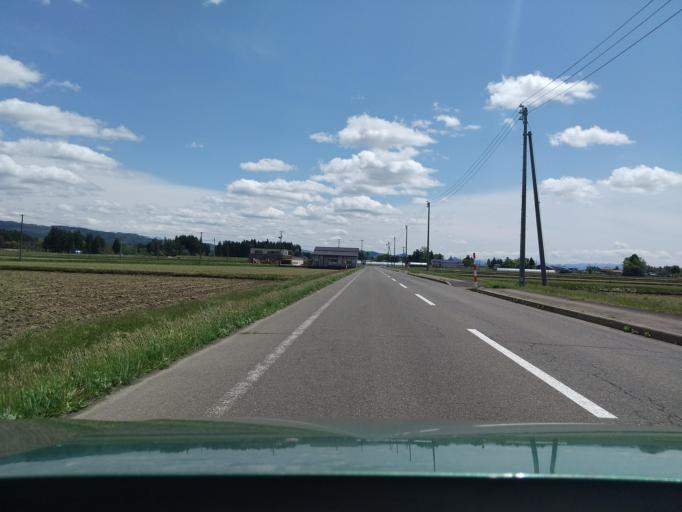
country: JP
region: Akita
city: Yokotemachi
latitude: 39.3623
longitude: 140.5369
